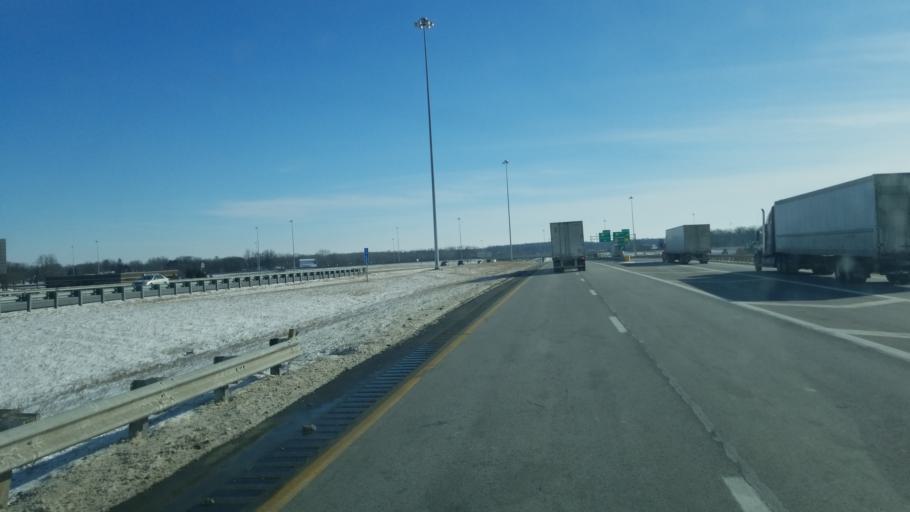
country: US
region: Ohio
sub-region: Lucas County
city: Maumee
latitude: 41.5585
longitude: -83.6879
